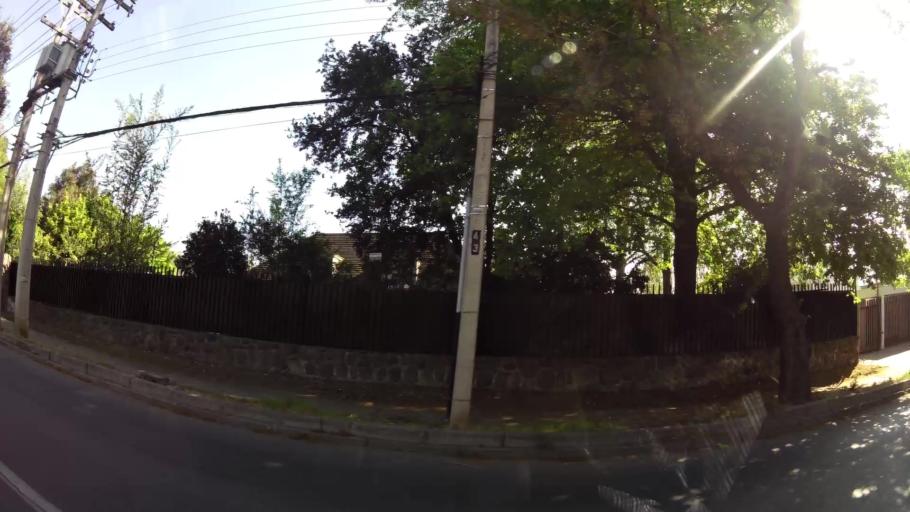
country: CL
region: Santiago Metropolitan
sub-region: Provincia de Santiago
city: Villa Presidente Frei, Nunoa, Santiago, Chile
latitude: -33.3805
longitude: -70.5129
